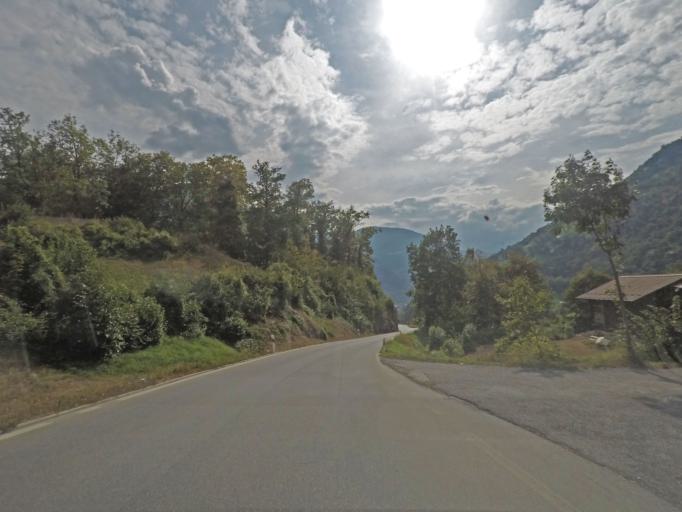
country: CH
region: Valais
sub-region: Brig District
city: Naters
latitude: 46.3323
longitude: 7.9929
